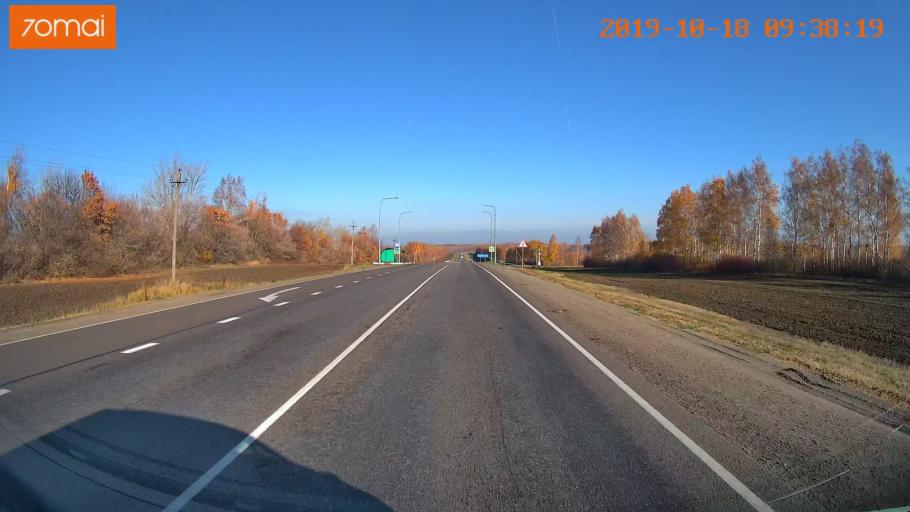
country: RU
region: Tula
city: Yefremov
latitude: 53.2362
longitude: 38.1375
